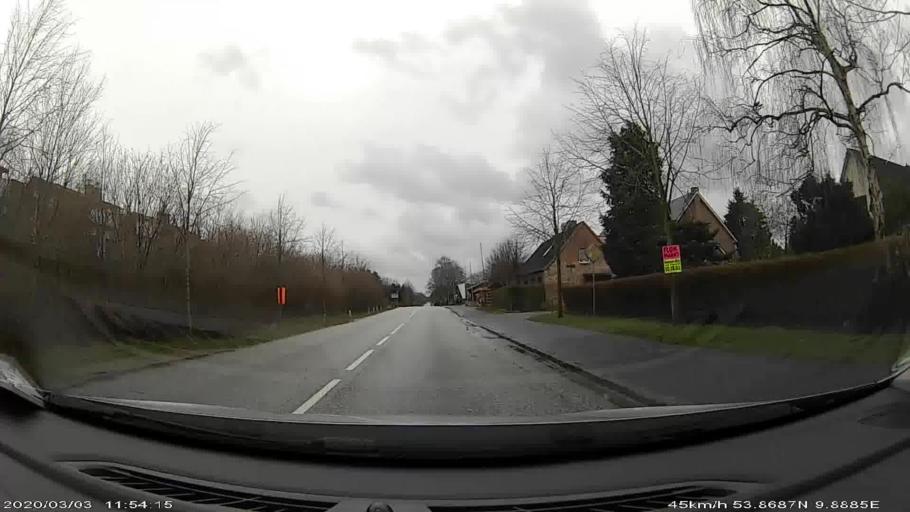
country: DE
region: Schleswig-Holstein
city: Lentfohrden
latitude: 53.8687
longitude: 9.8890
